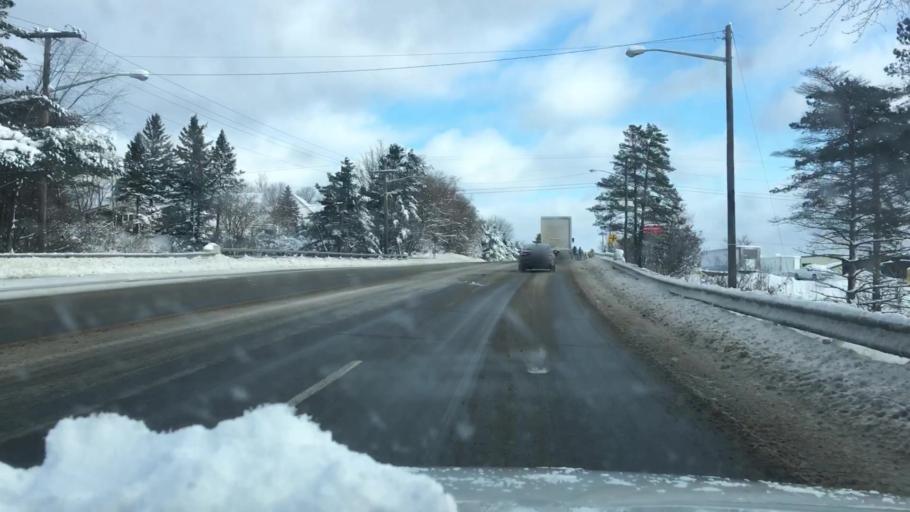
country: US
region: Maine
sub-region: Aroostook County
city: Caribou
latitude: 46.8572
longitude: -68.0055
